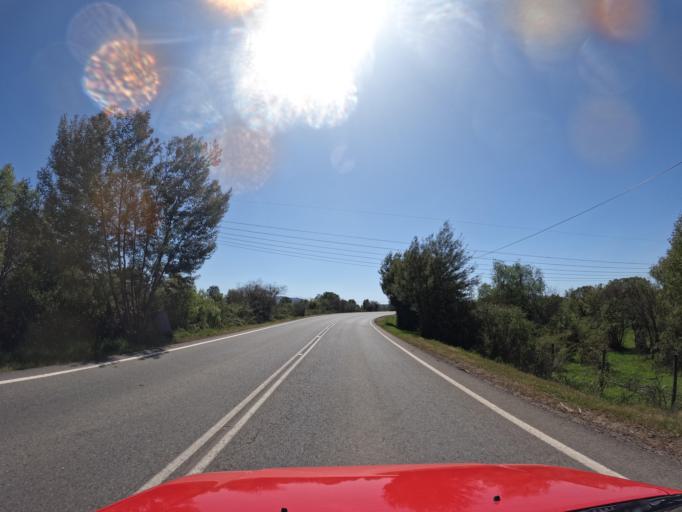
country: CL
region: Maule
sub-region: Provincia de Talca
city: San Clemente
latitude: -35.4789
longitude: -71.2698
